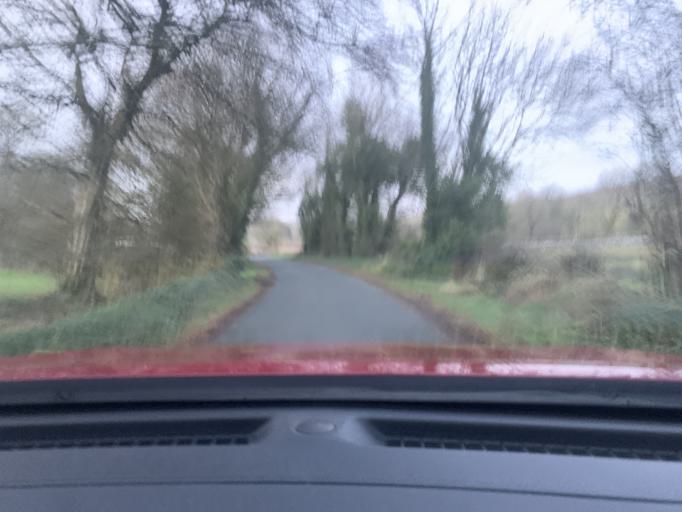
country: IE
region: Connaught
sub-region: Sligo
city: Ballymote
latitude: 54.0372
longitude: -8.4071
